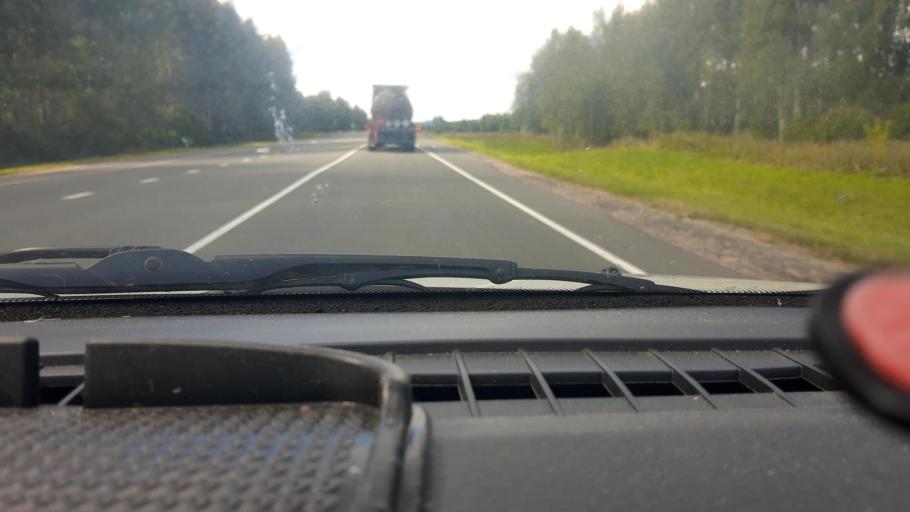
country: RU
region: Nizjnij Novgorod
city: Shatki
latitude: 55.1196
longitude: 44.2806
